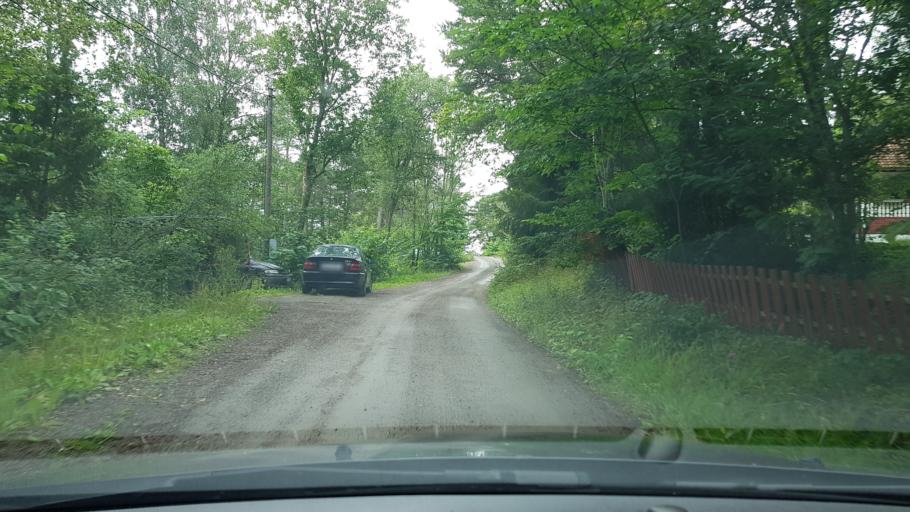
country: SE
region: Uppsala
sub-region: Uppsala Kommun
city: Alsike
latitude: 59.7207
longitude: 17.6979
